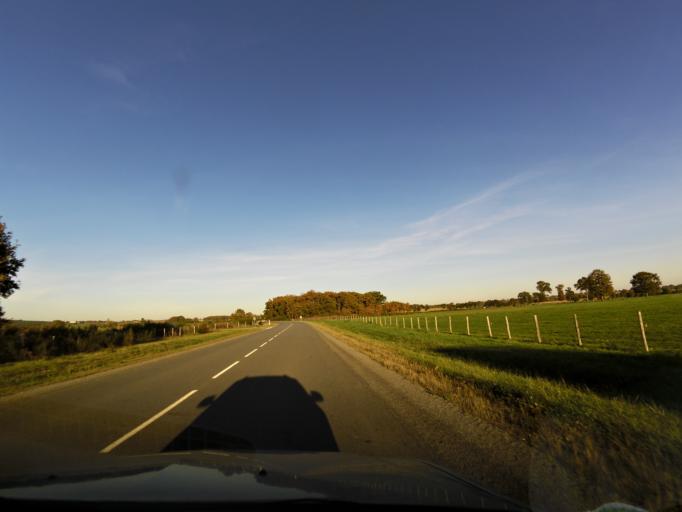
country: FR
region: Brittany
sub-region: Departement d'Ille-et-Vilaine
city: Crevin
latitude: 47.9090
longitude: -1.6776
